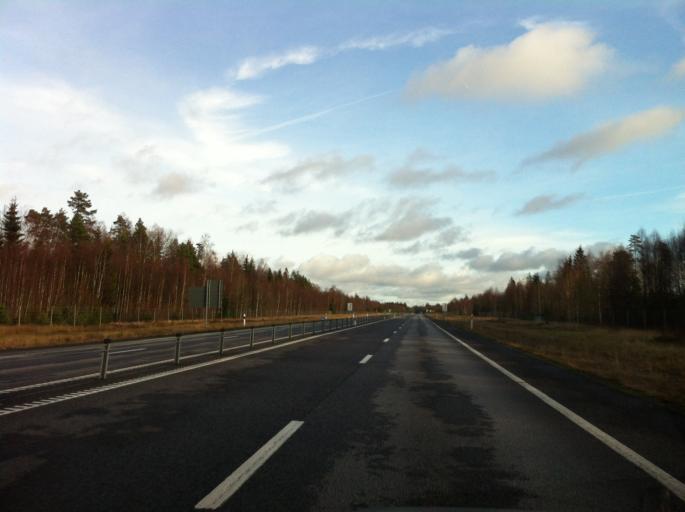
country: SE
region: Kronoberg
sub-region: Alvesta Kommun
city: Vislanda
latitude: 56.6732
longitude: 14.3132
